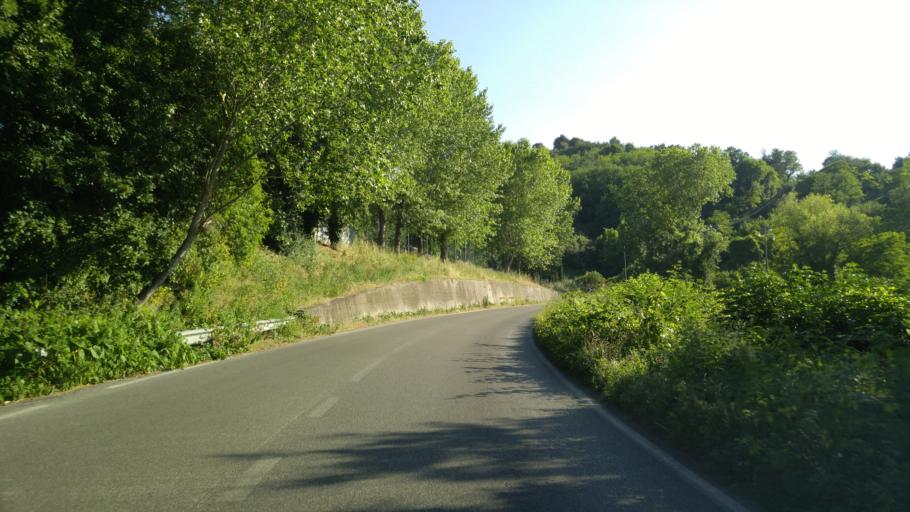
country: IT
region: The Marches
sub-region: Provincia di Pesaro e Urbino
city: Fenile
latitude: 43.8722
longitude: 12.9417
